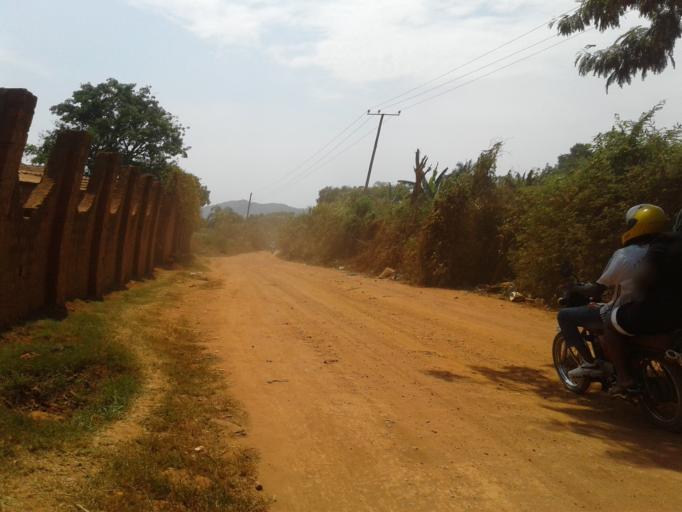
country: UG
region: Central Region
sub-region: Kampala District
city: Kampala
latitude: 0.2642
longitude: 32.6307
